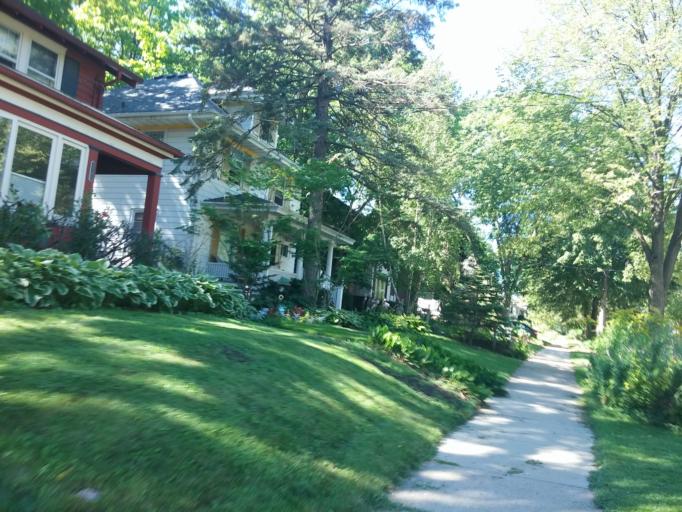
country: US
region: Wisconsin
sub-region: Dane County
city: Madison
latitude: 43.0650
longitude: -89.4186
